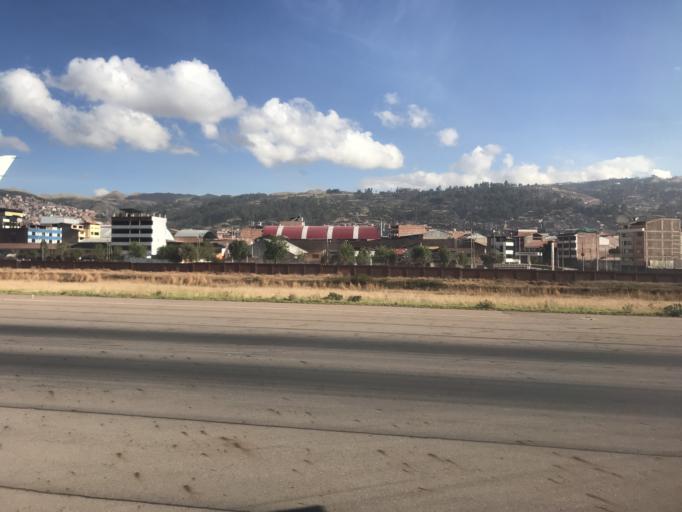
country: PE
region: Cusco
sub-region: Provincia de Cusco
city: Cusco
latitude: -13.5358
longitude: -71.9398
